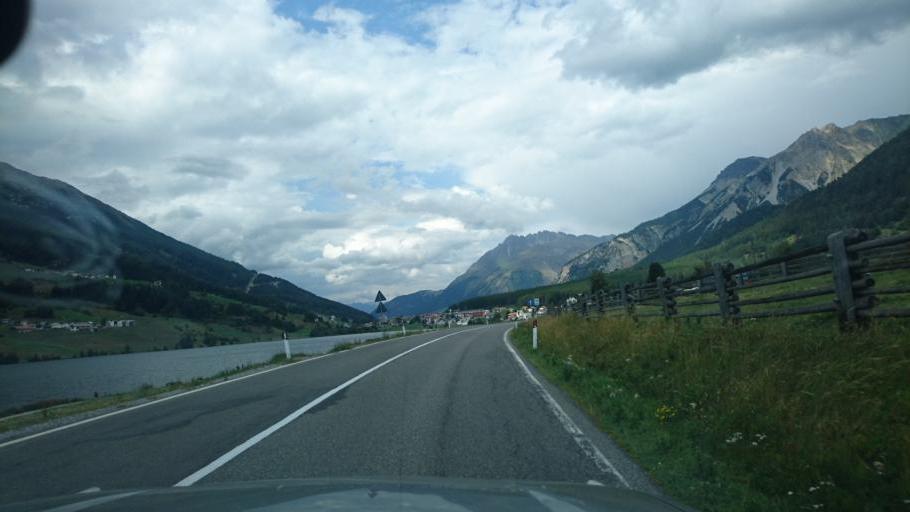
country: IT
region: Trentino-Alto Adige
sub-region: Bolzano
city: Curon Venosta
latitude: 46.7508
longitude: 10.5357
